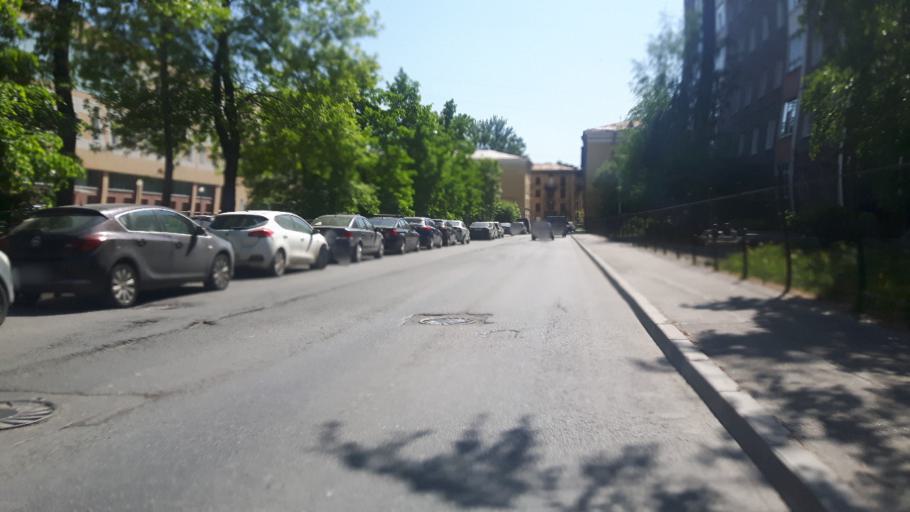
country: RU
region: St.-Petersburg
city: Admiralteisky
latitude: 59.9009
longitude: 30.2856
